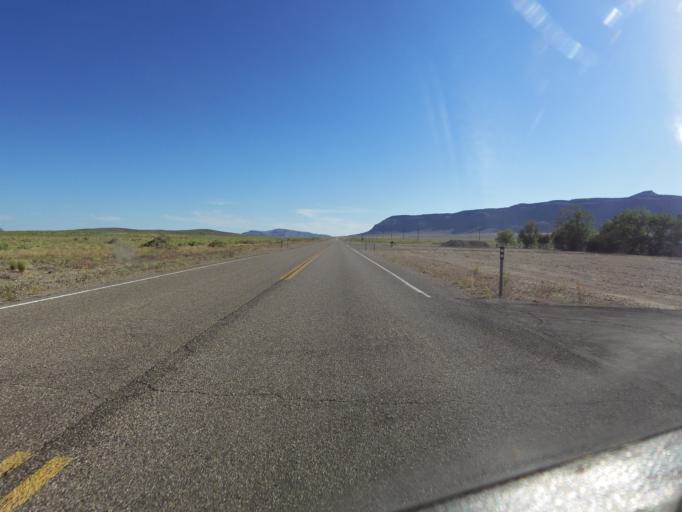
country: US
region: Nevada
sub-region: Nye County
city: Tonopah
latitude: 38.3717
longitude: -116.2270
